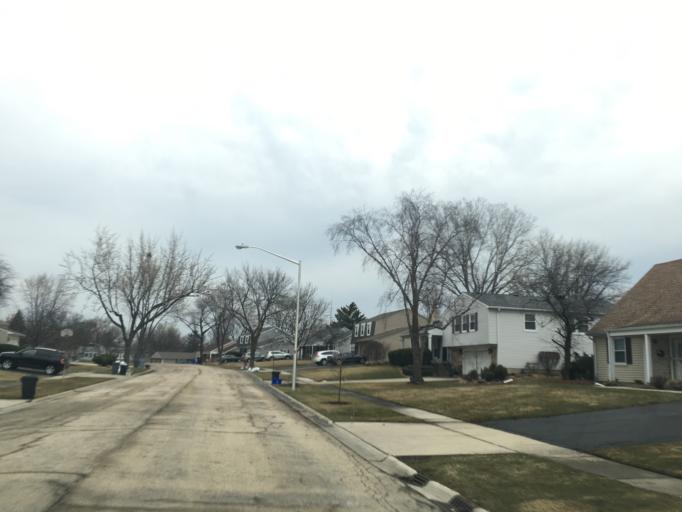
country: US
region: Illinois
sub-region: DuPage County
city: Hanover Park
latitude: 42.0293
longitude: -88.1243
